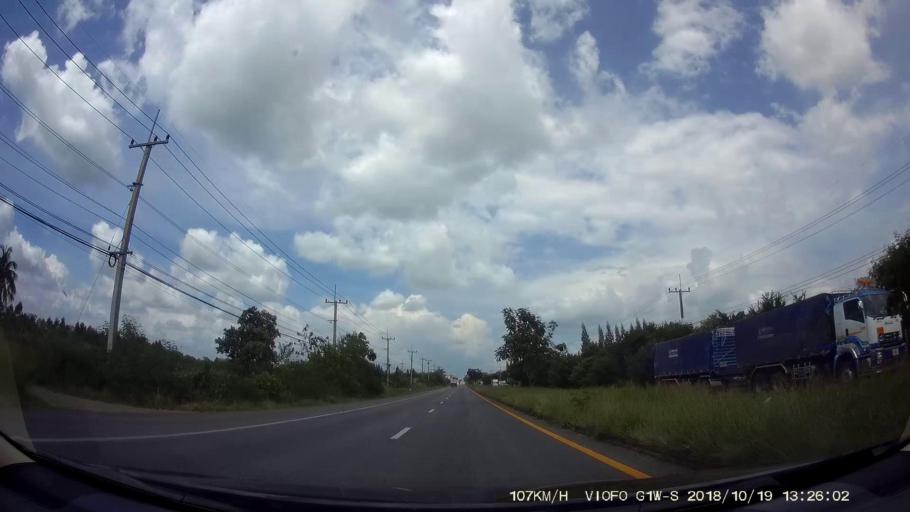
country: TH
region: Chaiyaphum
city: Chatturat
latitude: 15.5295
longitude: 101.8305
